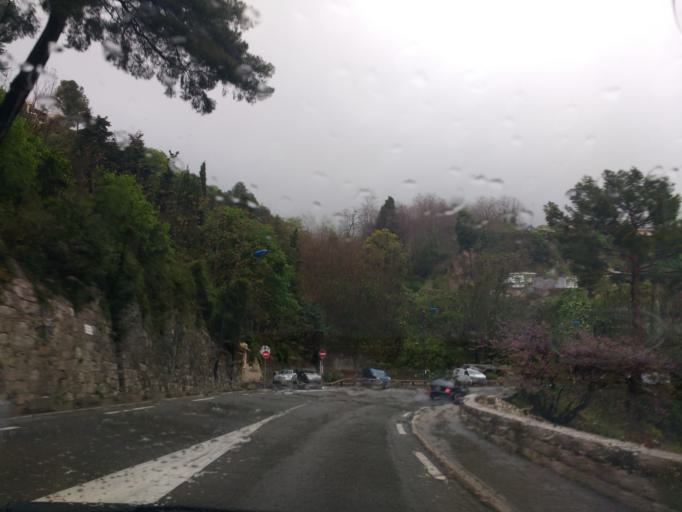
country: FR
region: Provence-Alpes-Cote d'Azur
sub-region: Departement des Alpes-Maritimes
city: Eze
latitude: 43.7243
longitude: 7.3799
